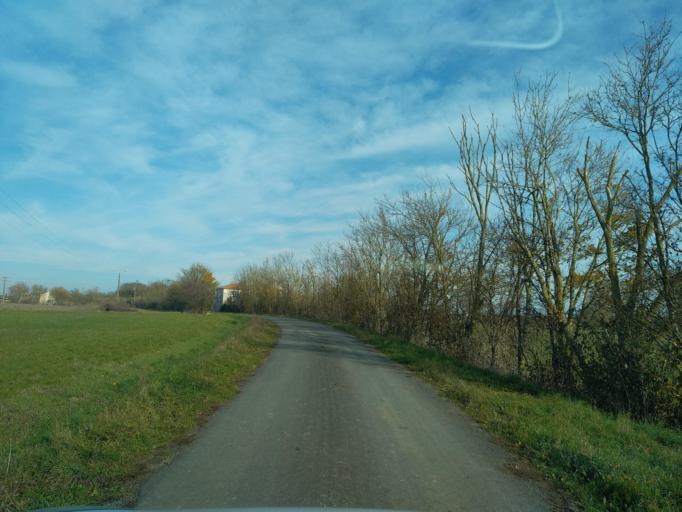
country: FR
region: Pays de la Loire
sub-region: Departement de la Vendee
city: Maillezais
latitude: 46.3539
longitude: -0.7429
